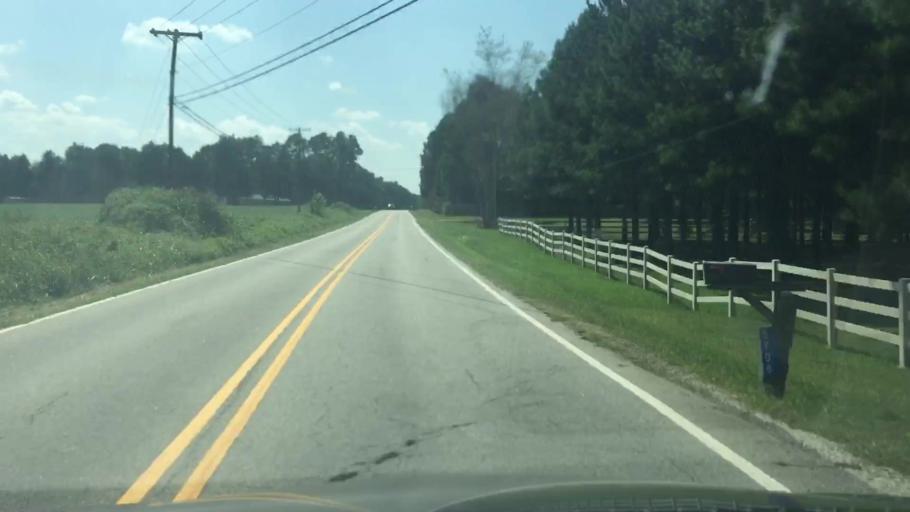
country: US
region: North Carolina
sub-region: Rowan County
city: China Grove
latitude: 35.6535
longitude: -80.5840
